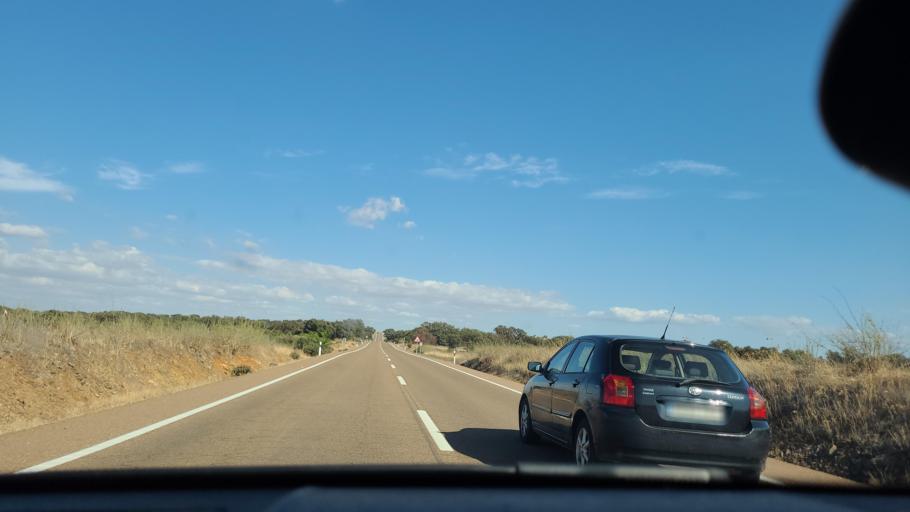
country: ES
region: Extremadura
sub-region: Provincia de Badajoz
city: Usagre
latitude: 38.3701
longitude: -6.2460
